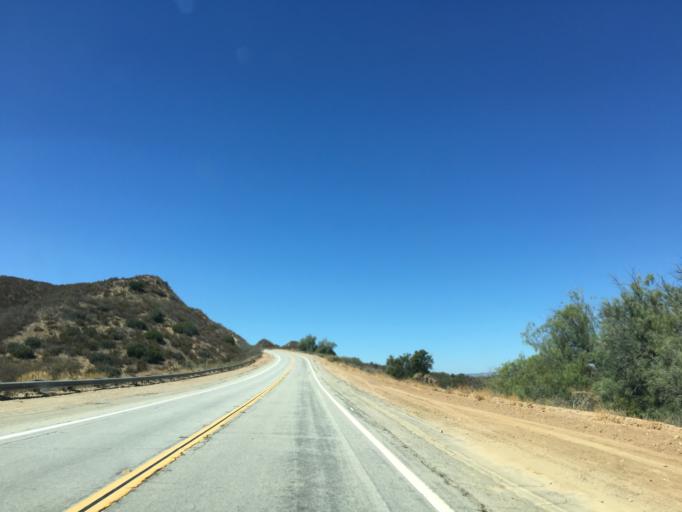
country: US
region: California
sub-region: Los Angeles County
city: Castaic
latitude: 34.5483
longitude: -118.5472
